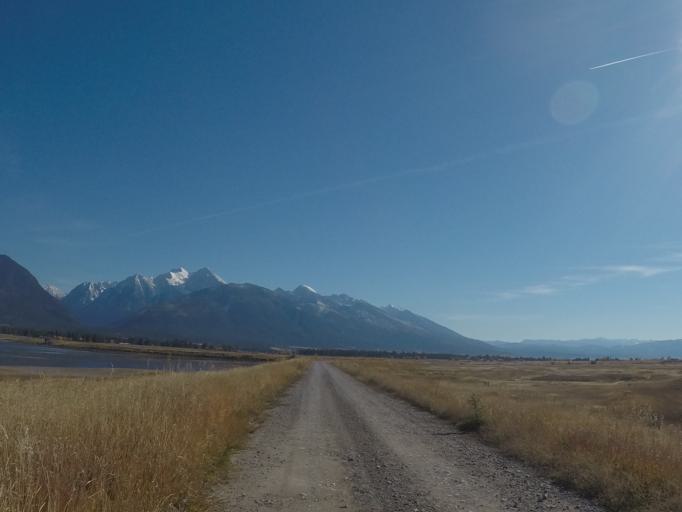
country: US
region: Montana
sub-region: Lake County
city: Ronan
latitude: 47.4563
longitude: -114.0859
